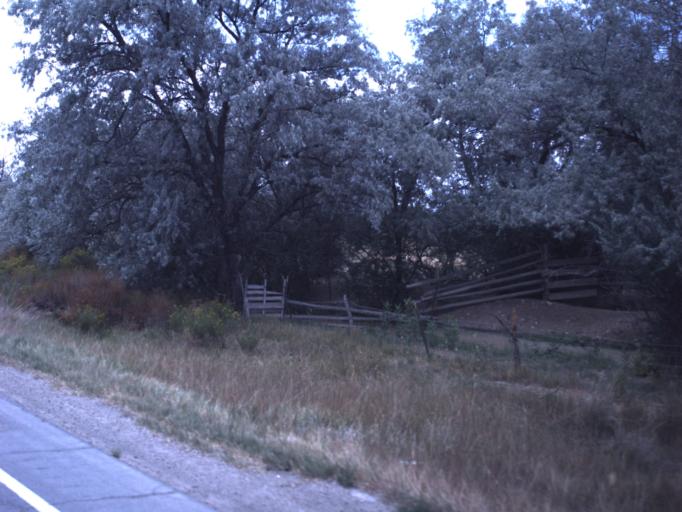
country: US
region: Utah
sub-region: Duchesne County
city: Roosevelt
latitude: 40.1938
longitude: -110.0739
